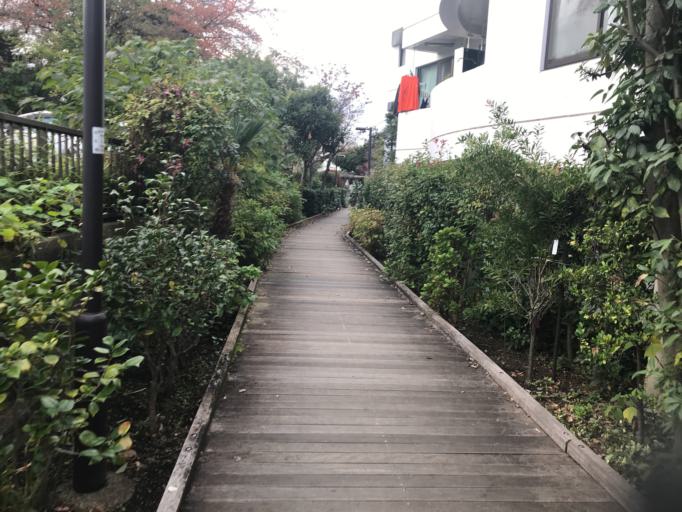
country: JP
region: Tokyo
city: Tokyo
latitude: 35.6097
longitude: 139.6606
